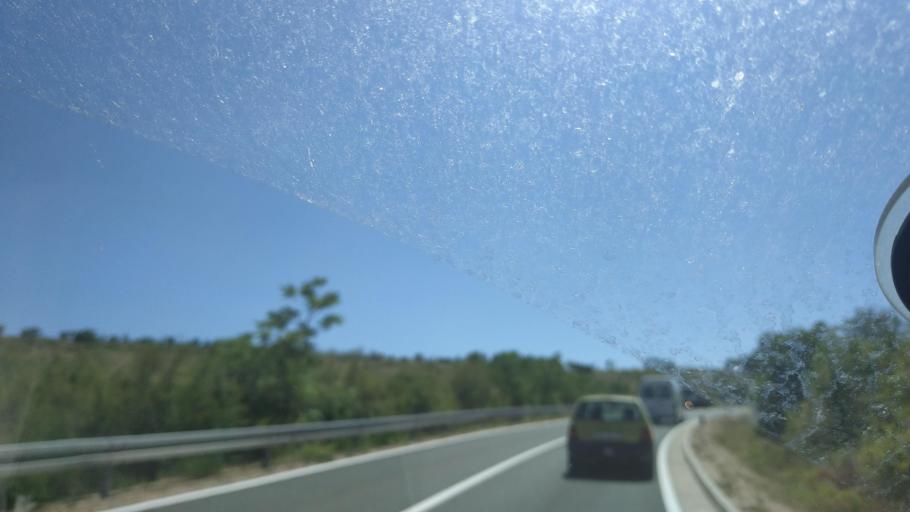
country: HR
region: Sibensko-Kniniska
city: Drnis
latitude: 43.8518
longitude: 16.1565
